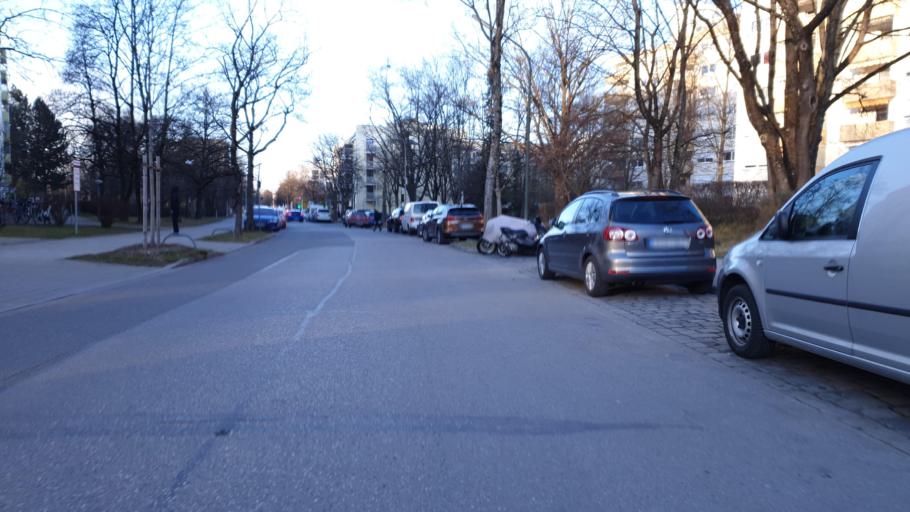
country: DE
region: Bavaria
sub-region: Upper Bavaria
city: Pasing
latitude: 48.1480
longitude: 11.4392
